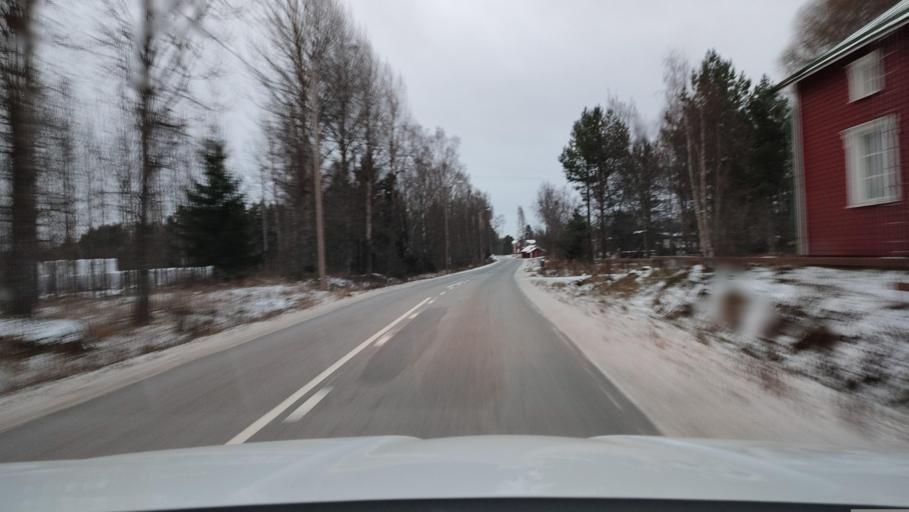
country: FI
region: Ostrobothnia
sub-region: Vaasa
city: Replot
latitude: 63.3420
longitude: 21.3295
